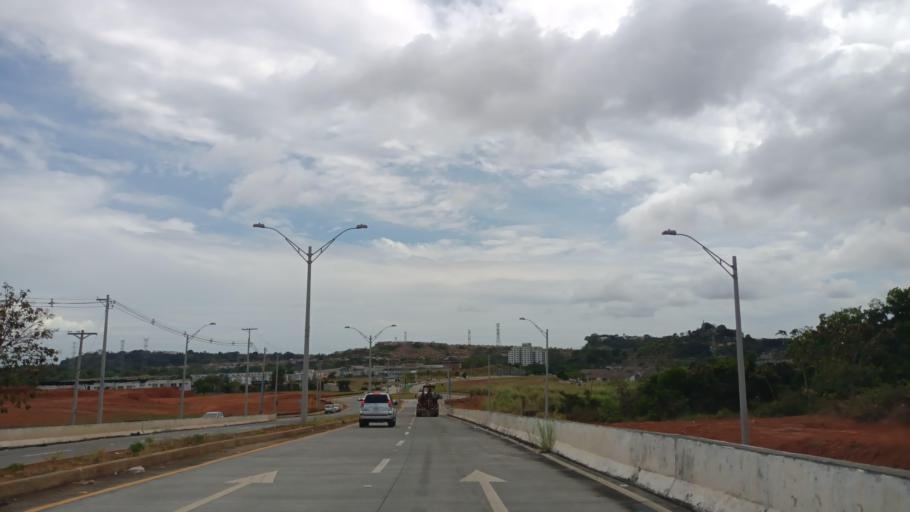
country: PA
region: Panama
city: San Miguelito
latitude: 9.0900
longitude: -79.4621
